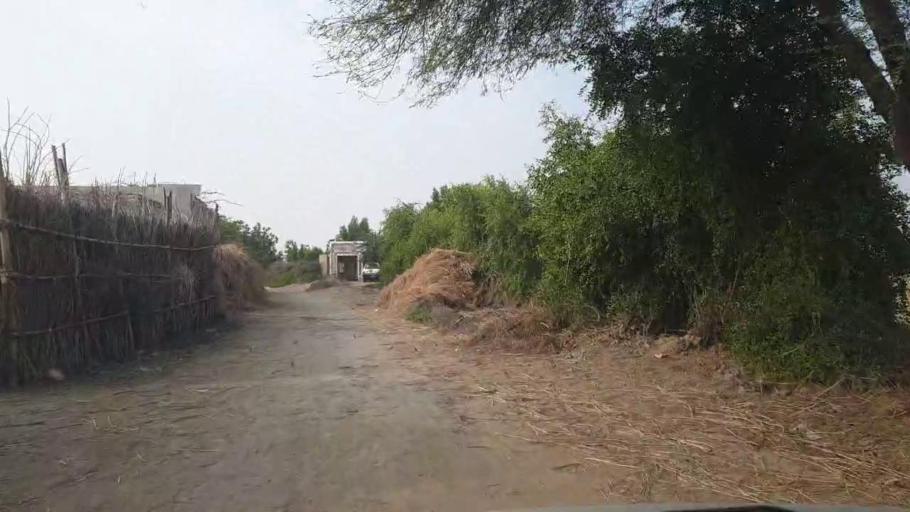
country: PK
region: Sindh
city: Matli
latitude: 25.0386
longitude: 68.7427
